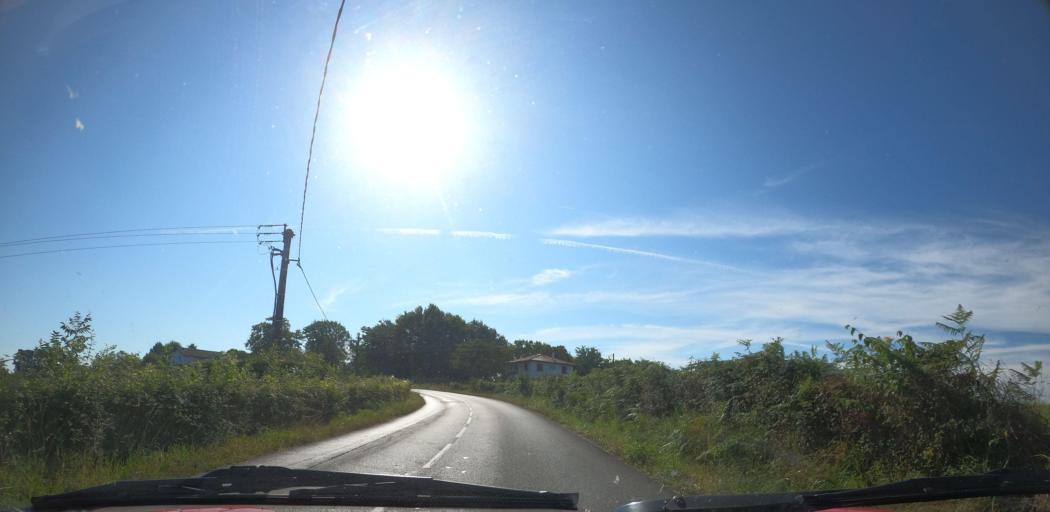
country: FR
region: Aquitaine
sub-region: Departement des Pyrenees-Atlantiques
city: Arbonne
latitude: 43.4067
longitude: -1.5430
